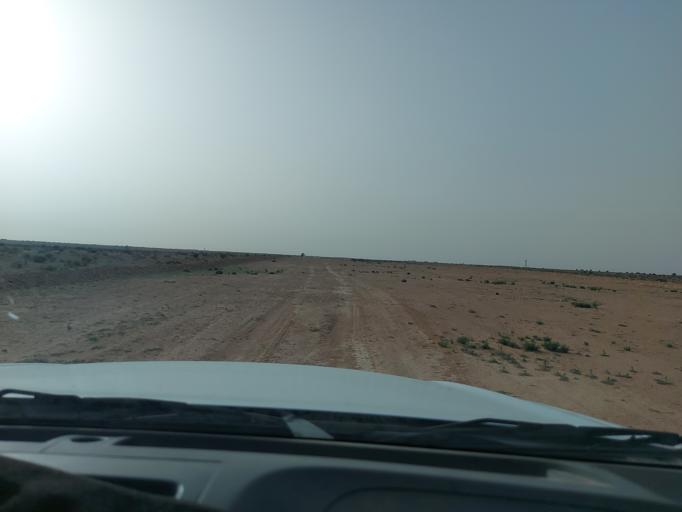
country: TN
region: Madanin
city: Medenine
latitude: 33.3433
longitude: 10.5924
